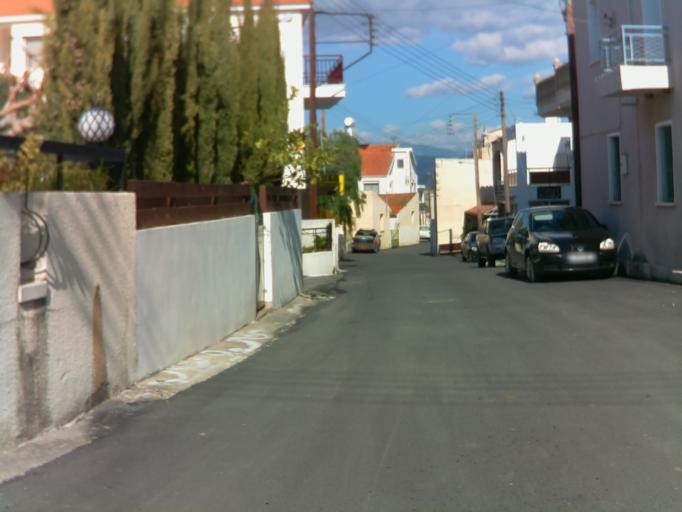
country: CY
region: Limassol
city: Pissouri
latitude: 34.6692
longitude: 32.7002
